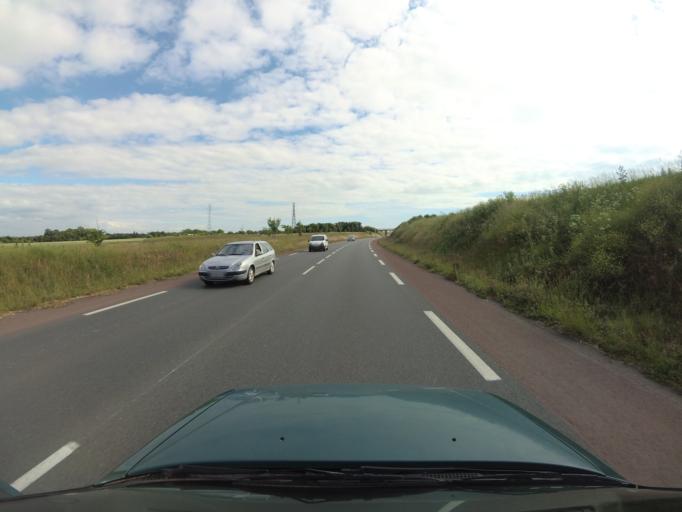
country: FR
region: Poitou-Charentes
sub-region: Departement de la Charente-Maritime
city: Saint-Xandre
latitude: 46.2070
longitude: -1.0893
